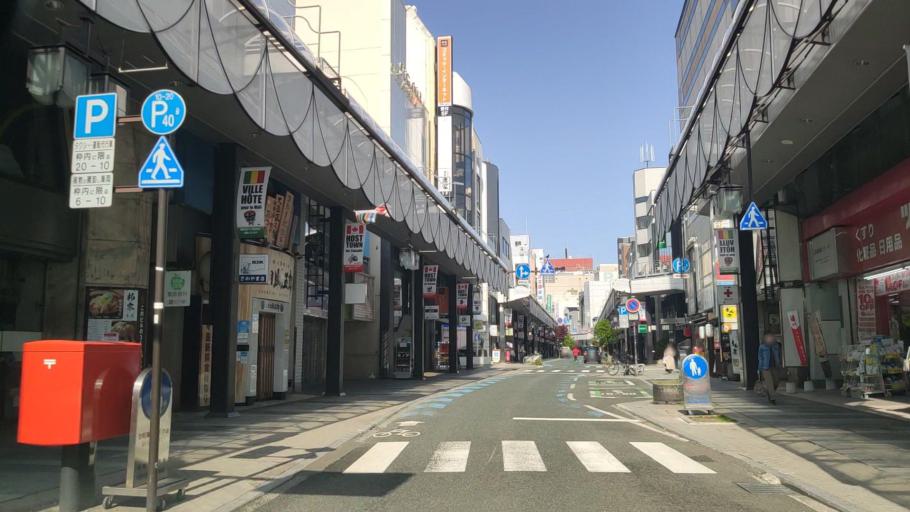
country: JP
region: Iwate
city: Morioka-shi
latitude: 39.7031
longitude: 141.1469
